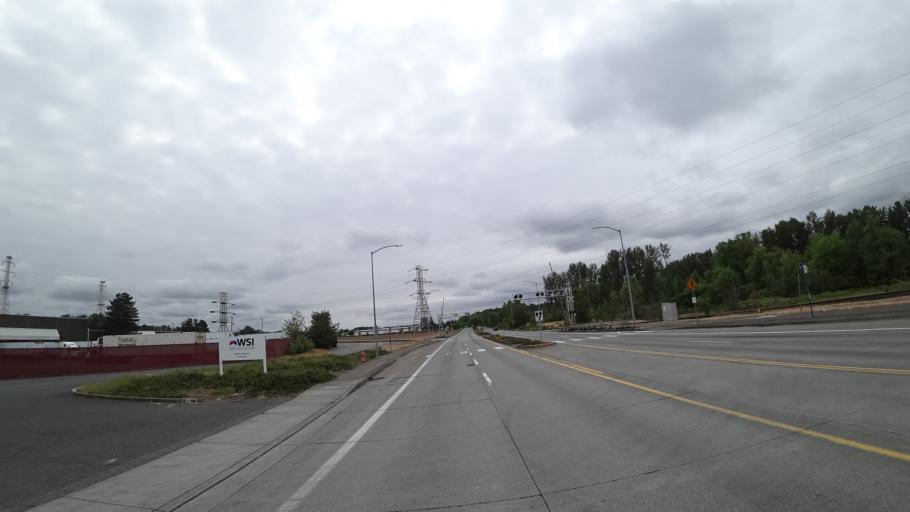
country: US
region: Washington
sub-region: Clark County
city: Vancouver
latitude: 45.6230
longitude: -122.7318
